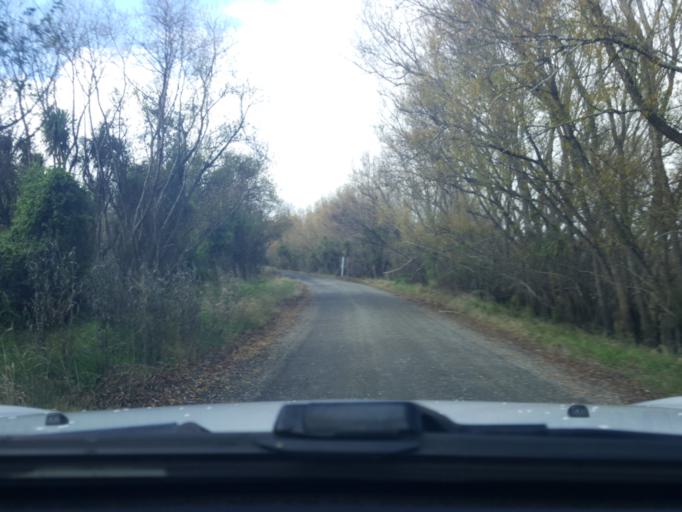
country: NZ
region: Waikato
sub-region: Waikato District
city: Te Kauwhata
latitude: -37.4104
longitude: 175.0588
